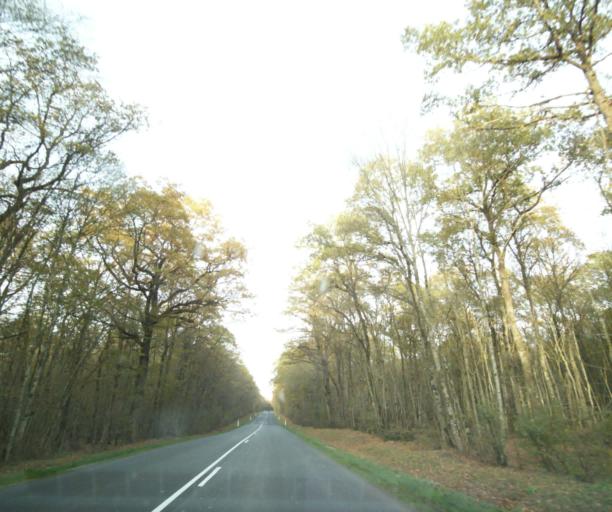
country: FR
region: Lorraine
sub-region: Departement de la Meuse
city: Etain
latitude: 49.1618
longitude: 5.6309
